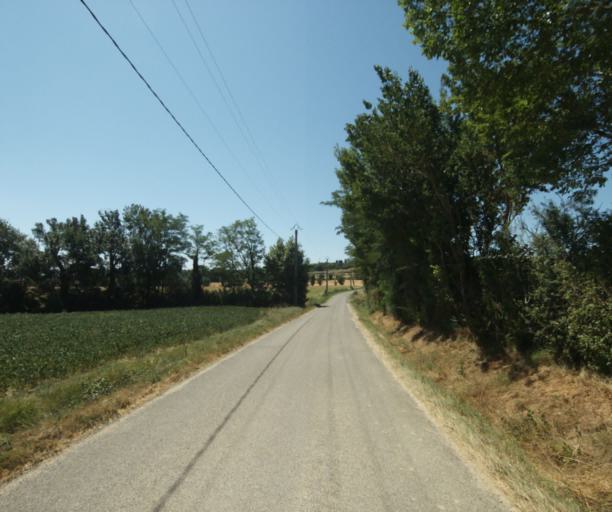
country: FR
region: Midi-Pyrenees
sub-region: Departement de la Haute-Garonne
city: Saint-Felix-Lauragais
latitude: 43.4860
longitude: 1.9286
